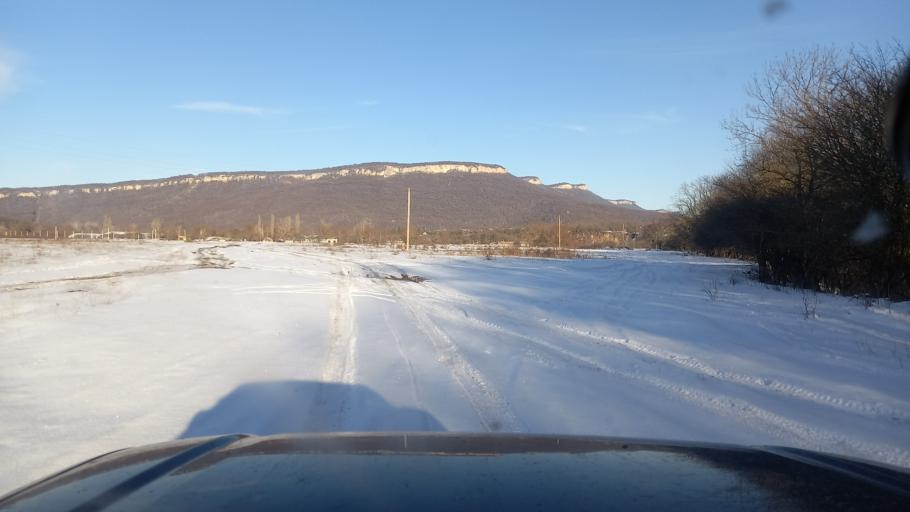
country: RU
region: Adygeya
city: Kamennomostskiy
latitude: 44.2182
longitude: 40.1786
